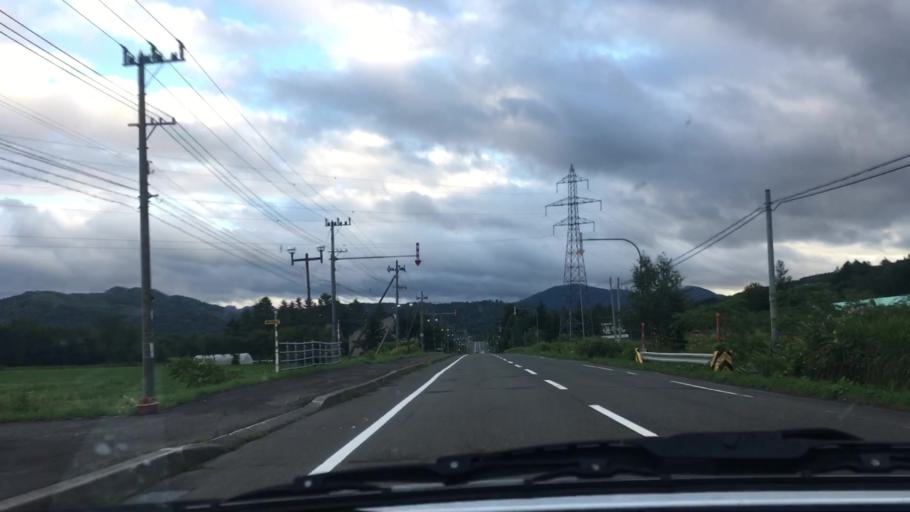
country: JP
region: Hokkaido
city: Shimo-furano
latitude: 42.9984
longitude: 142.4046
